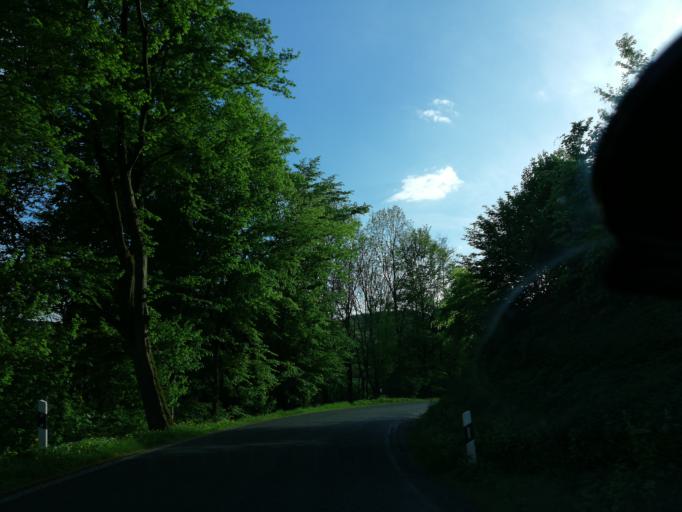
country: DE
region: North Rhine-Westphalia
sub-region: Regierungsbezirk Detmold
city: Dorentrup
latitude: 52.1346
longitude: 8.9820
